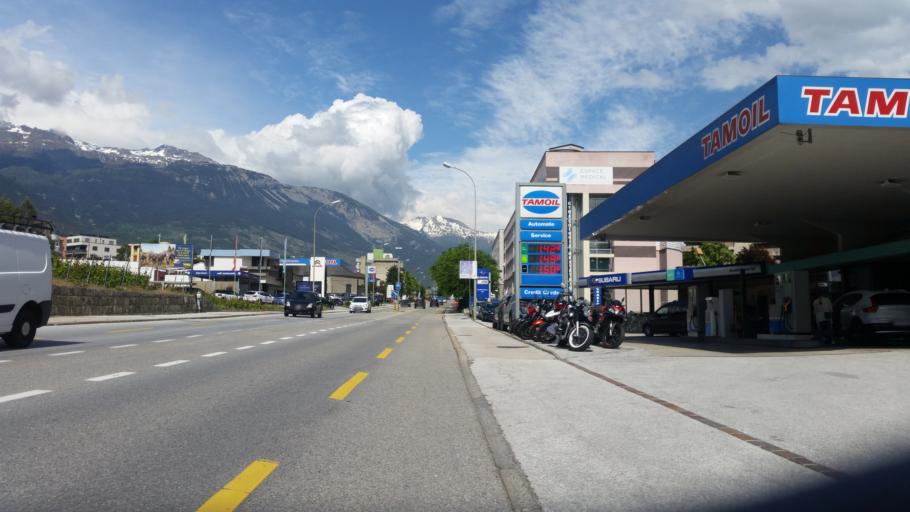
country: CH
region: Valais
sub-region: Sierre District
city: Chalais
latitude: 46.2850
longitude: 7.5168
